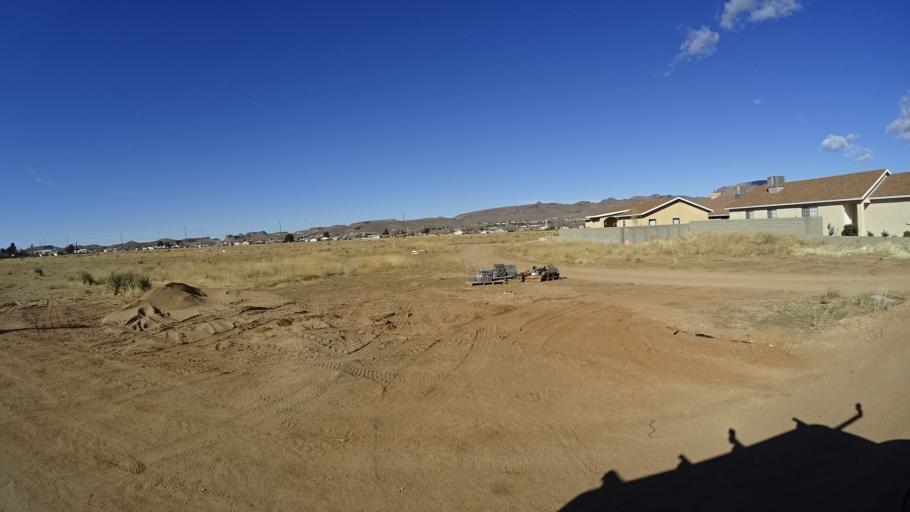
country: US
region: Arizona
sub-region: Mohave County
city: New Kingman-Butler
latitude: 35.2312
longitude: -114.0123
